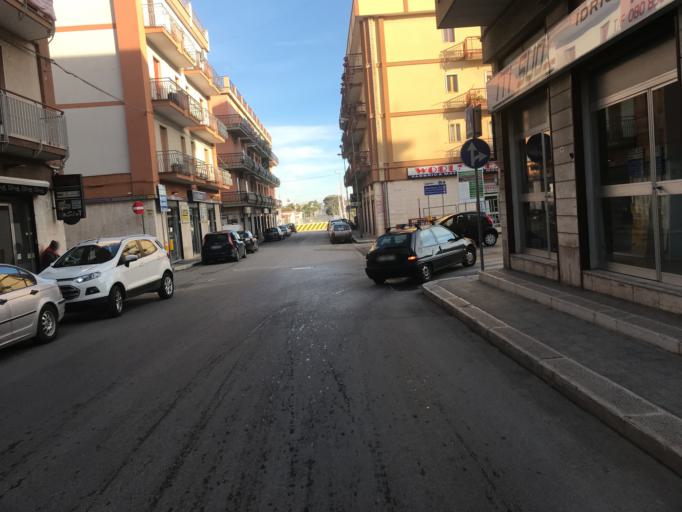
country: IT
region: Apulia
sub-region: Provincia di Bari
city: Corato
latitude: 41.1508
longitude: 16.4184
